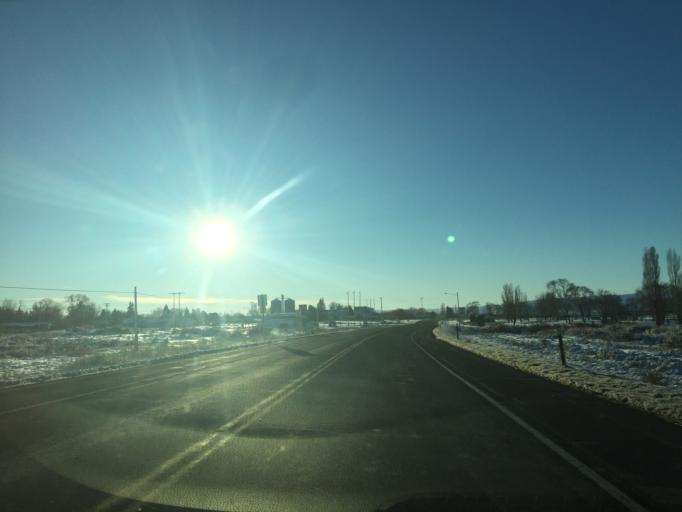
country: US
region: Washington
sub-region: Grant County
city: Soap Lake
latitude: 47.6181
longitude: -119.2856
